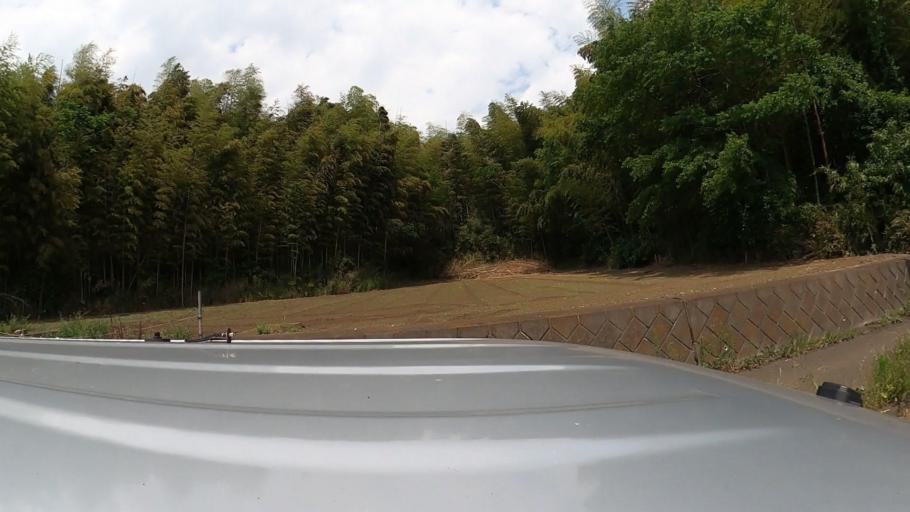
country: JP
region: Kanagawa
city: Chigasaki
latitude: 35.3851
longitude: 139.4209
